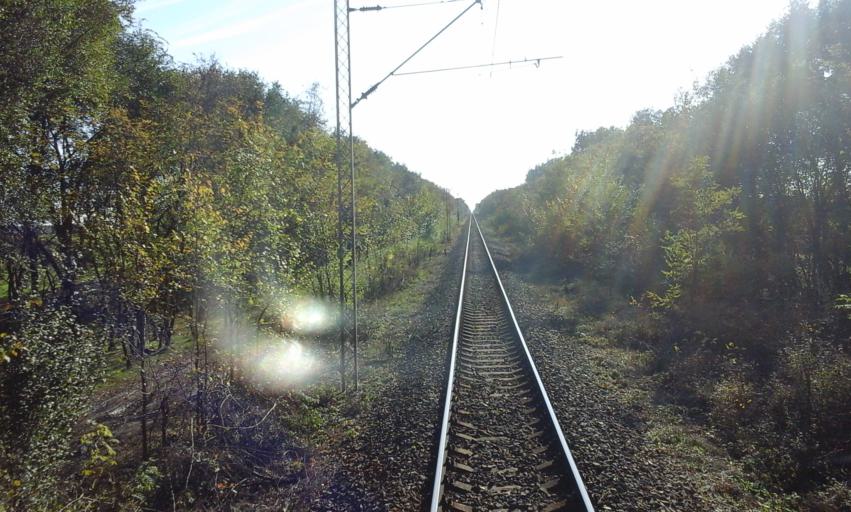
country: RS
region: Autonomna Pokrajina Vojvodina
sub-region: Severnobacki Okrug
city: Backa Topola
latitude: 45.8562
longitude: 19.6554
